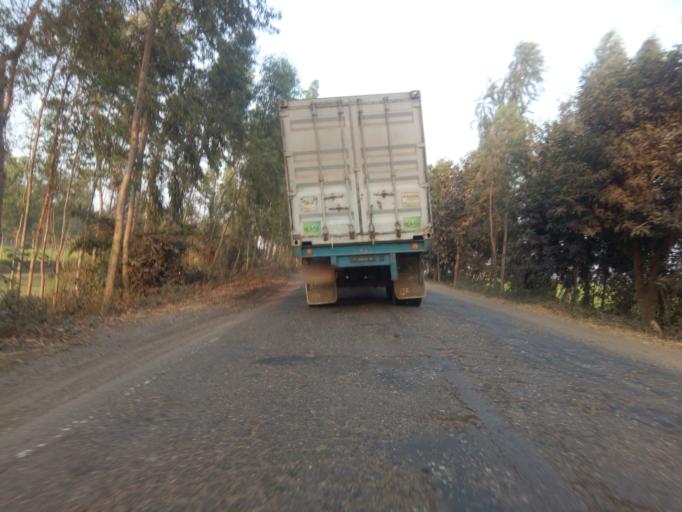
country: BD
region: Rajshahi
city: Bogra
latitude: 24.5605
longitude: 89.2025
